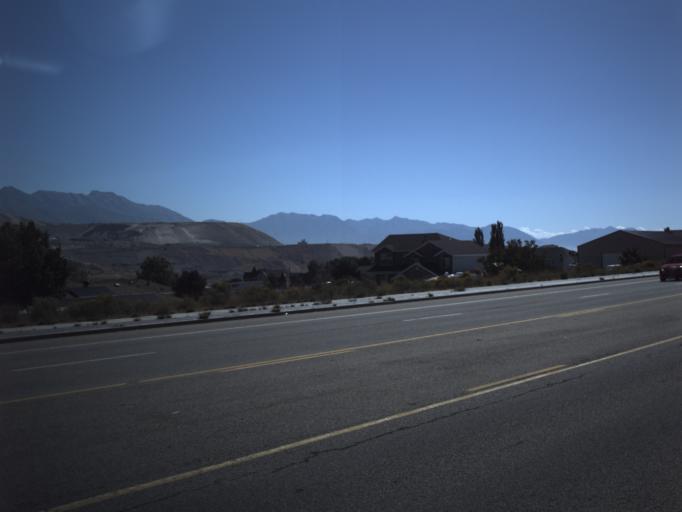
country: US
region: Utah
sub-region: Salt Lake County
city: Bluffdale
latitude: 40.4669
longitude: -111.9449
